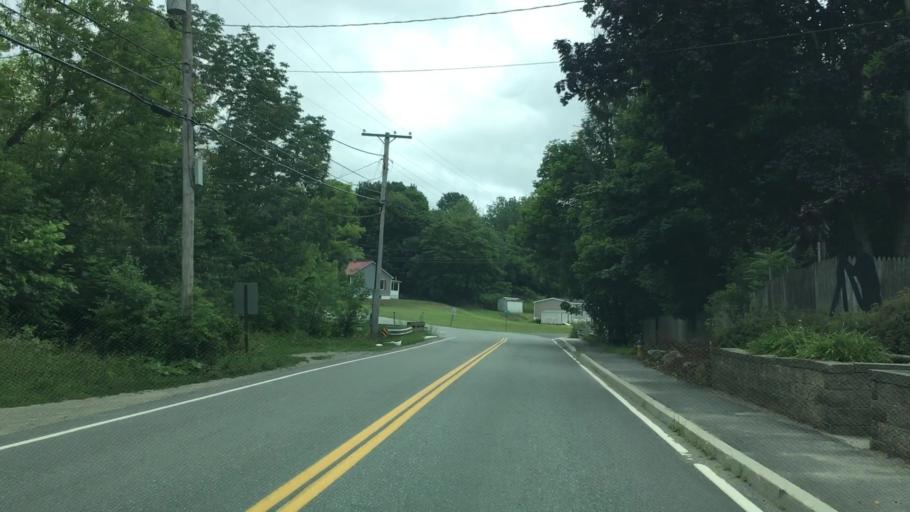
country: US
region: Maine
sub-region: Penobscot County
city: Bangor
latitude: 44.7672
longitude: -68.7803
